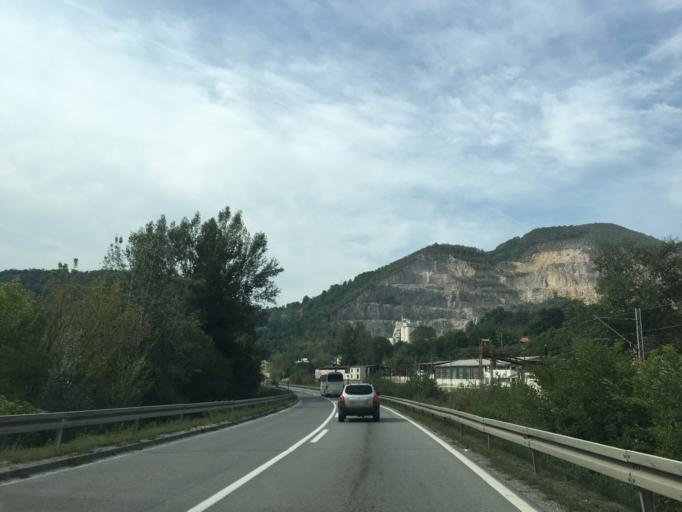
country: RS
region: Central Serbia
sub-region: Moravicki Okrug
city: Lucani
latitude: 43.8948
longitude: 20.1227
